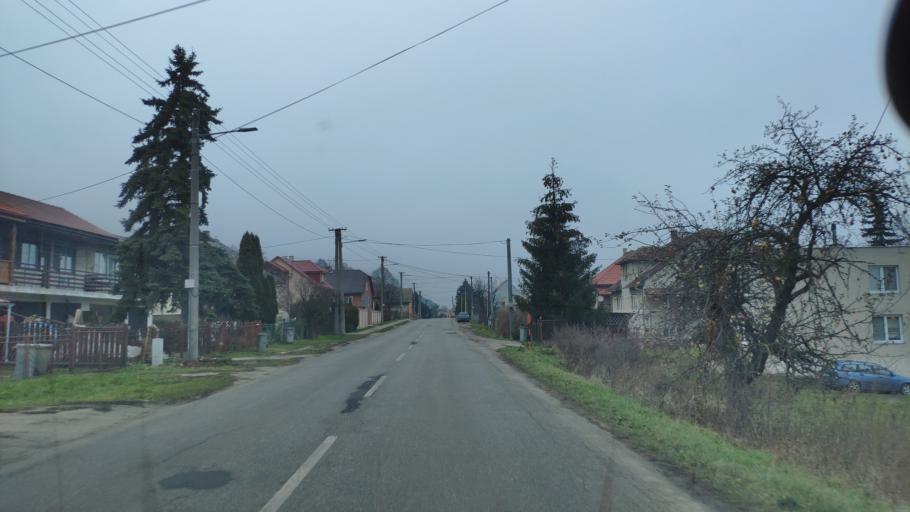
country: SK
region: Kosicky
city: Dobsina
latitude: 48.6512
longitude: 20.3675
